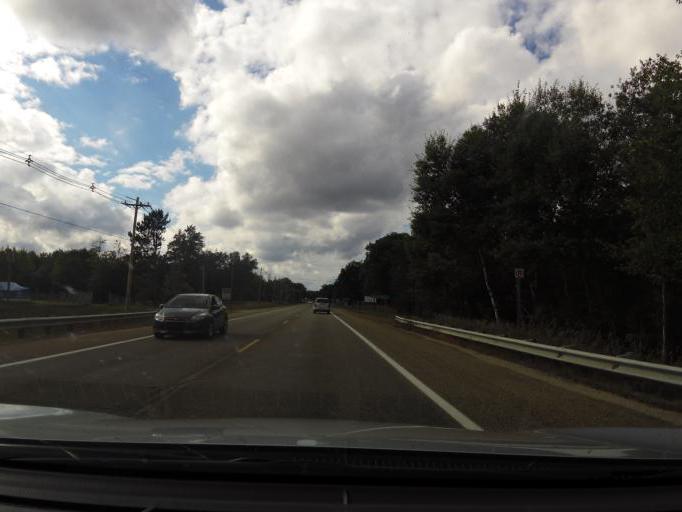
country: US
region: Michigan
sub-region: Roscommon County
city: Prudenville
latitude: 44.3057
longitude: -84.6305
